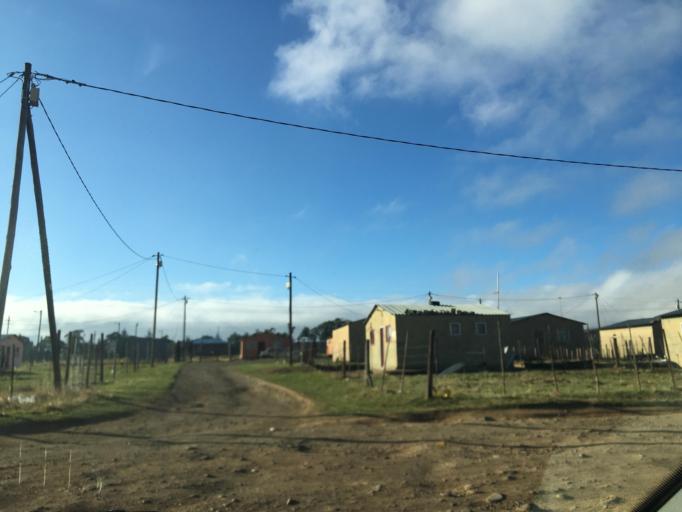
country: ZA
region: Eastern Cape
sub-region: Chris Hani District Municipality
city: Elliot
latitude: -31.3341
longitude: 27.8338
